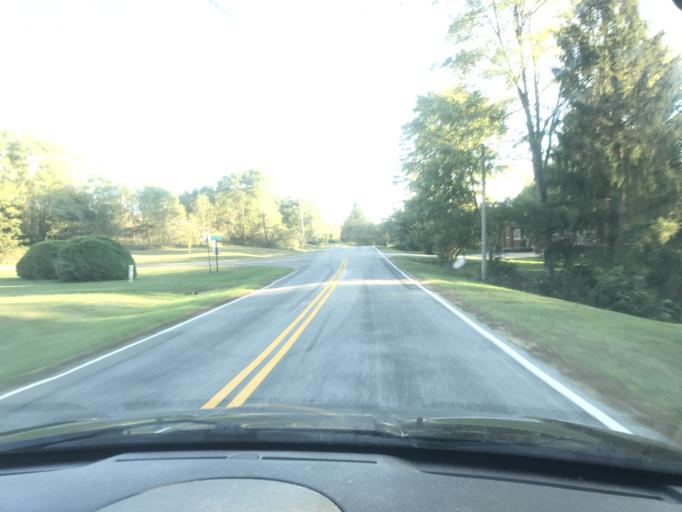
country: US
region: Ohio
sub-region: Logan County
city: De Graff
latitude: 40.2478
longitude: -83.8660
